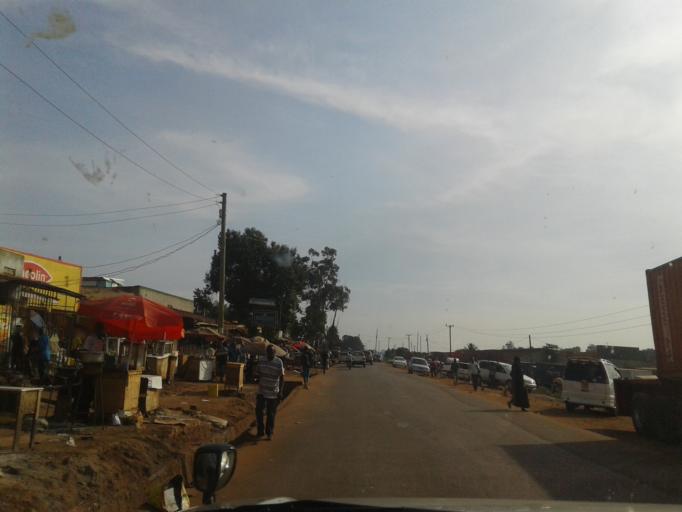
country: UG
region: Central Region
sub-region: Wakiso District
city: Kireka
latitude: 0.3323
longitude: 32.6230
